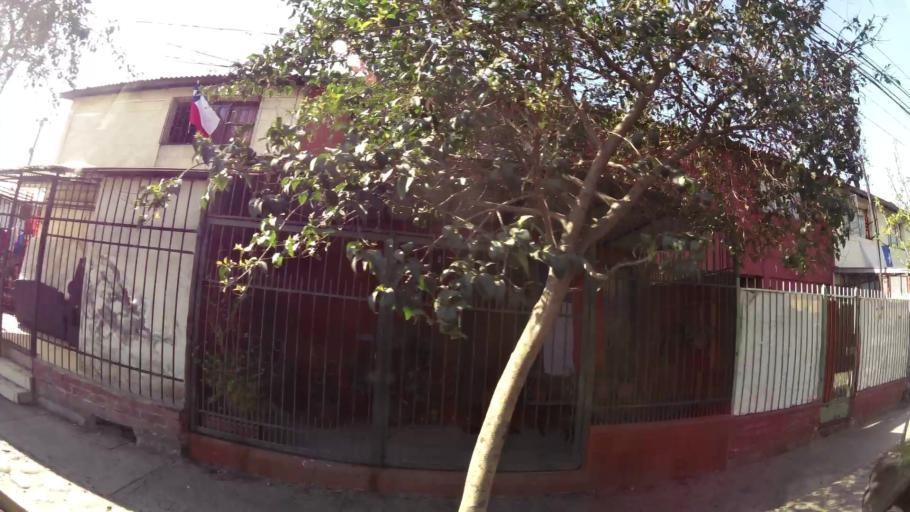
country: CL
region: Santiago Metropolitan
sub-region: Provincia de Santiago
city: Villa Presidente Frei, Nunoa, Santiago, Chile
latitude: -33.4805
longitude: -70.5698
